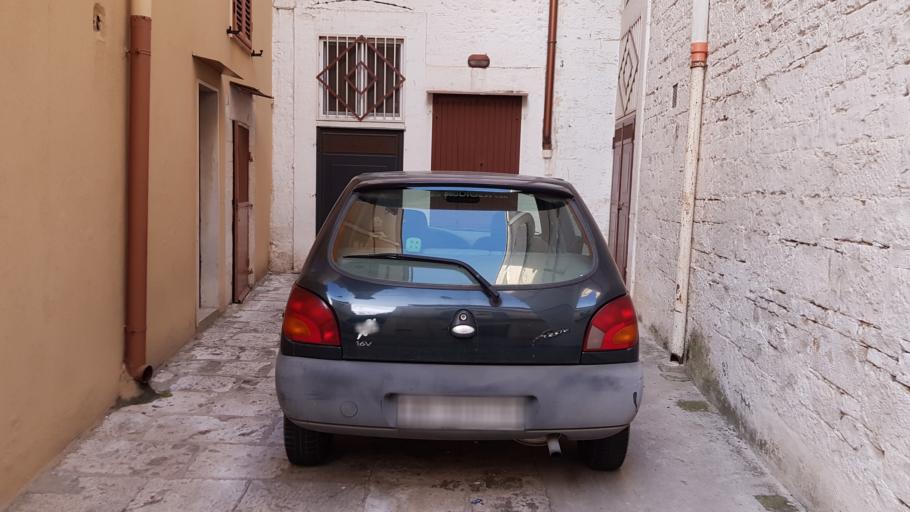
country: IT
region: Apulia
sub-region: Provincia di Bari
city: Ruvo di Puglia
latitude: 41.1192
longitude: 16.4835
